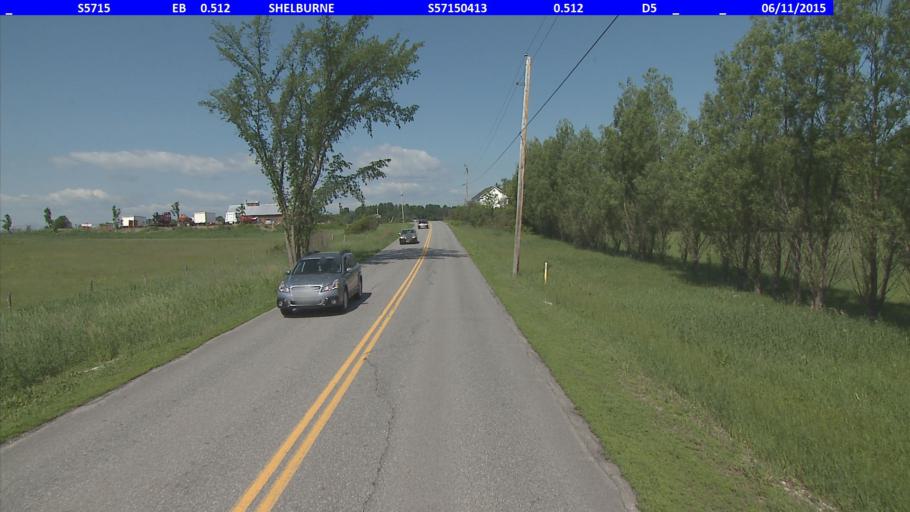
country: US
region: Vermont
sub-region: Chittenden County
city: Hinesburg
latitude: 44.3654
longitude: -73.1706
